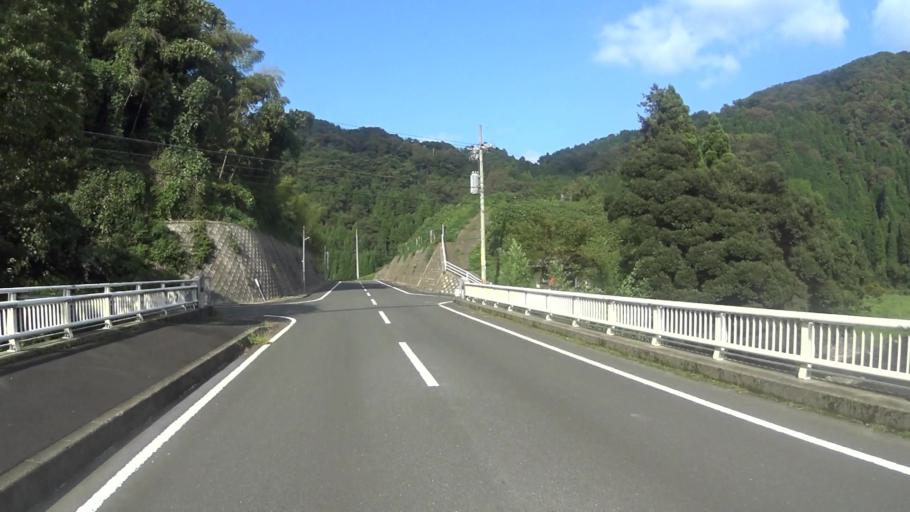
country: JP
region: Kyoto
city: Miyazu
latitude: 35.7289
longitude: 135.1627
